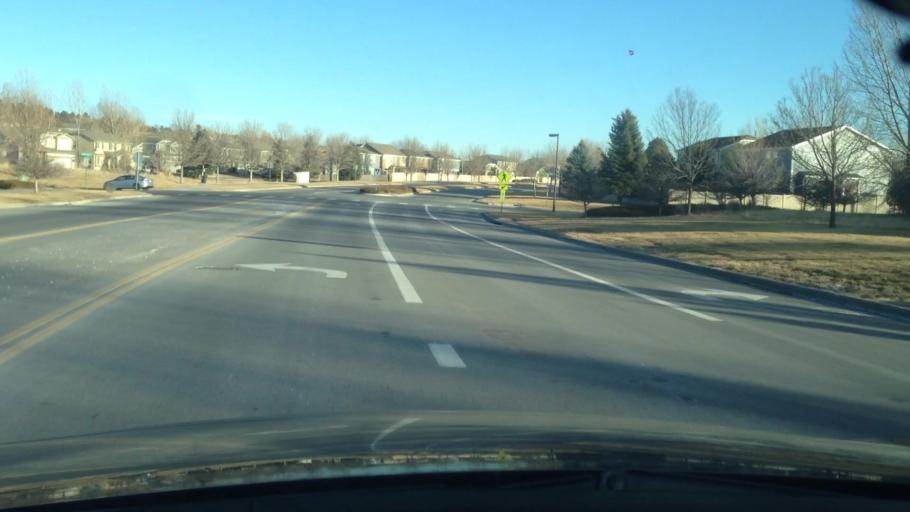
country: US
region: Colorado
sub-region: Douglas County
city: The Pinery
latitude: 39.4368
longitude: -104.7653
